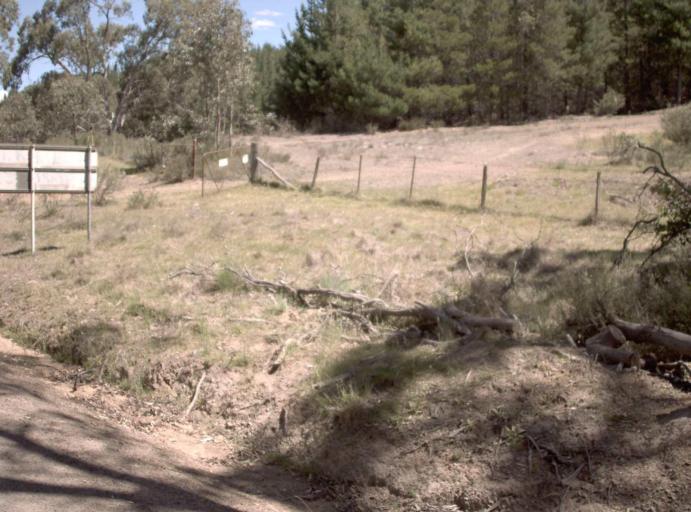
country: AU
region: New South Wales
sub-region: Bombala
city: Bombala
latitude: -37.1210
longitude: 148.6610
